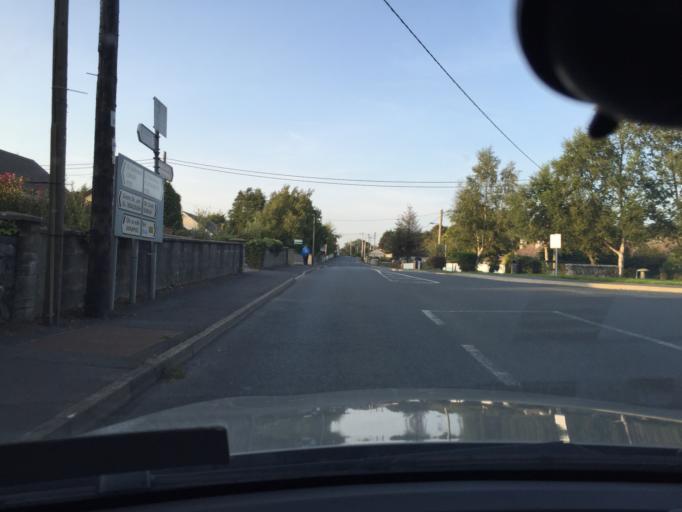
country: IE
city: Newtownmountkennedy
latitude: 53.0674
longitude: -6.2238
